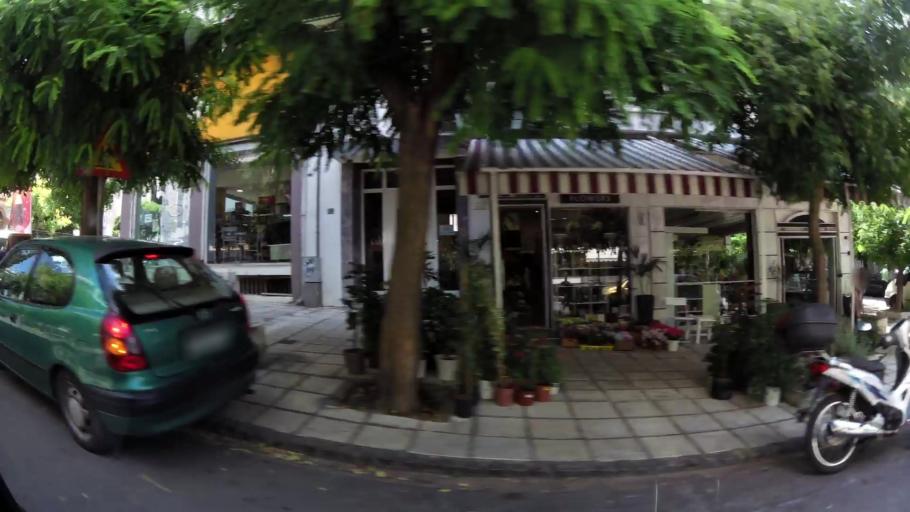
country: GR
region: Central Macedonia
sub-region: Nomos Thessalonikis
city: Triandria
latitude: 40.6181
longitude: 22.9745
